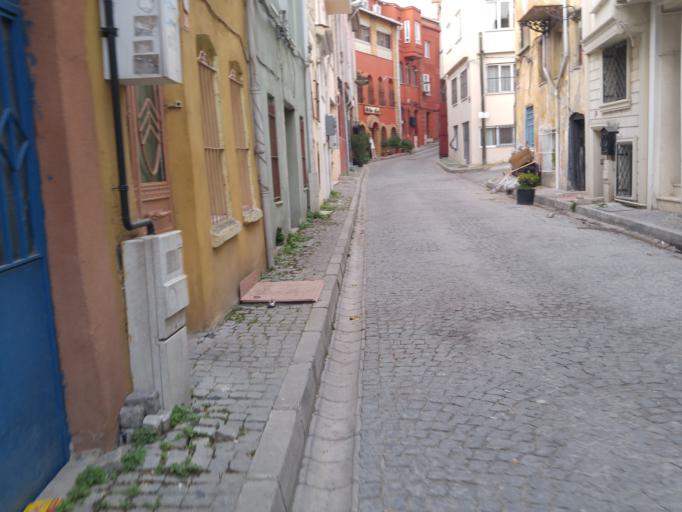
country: TR
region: Istanbul
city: Eminoenue
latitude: 41.0031
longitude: 28.9767
